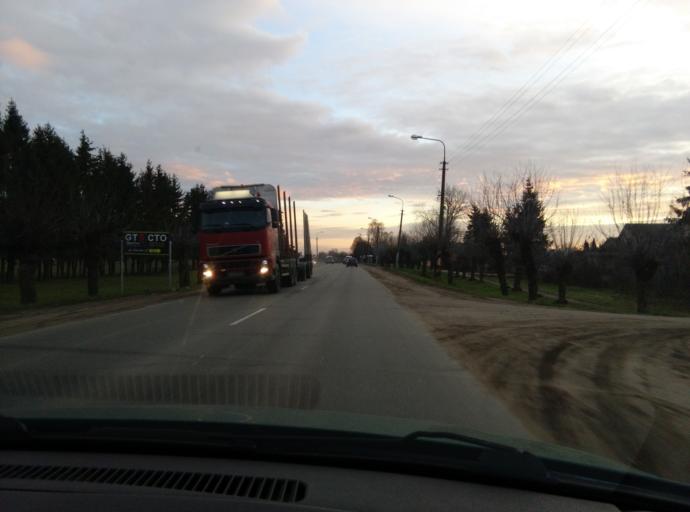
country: BY
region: Minsk
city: Horad Barysaw
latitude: 54.2681
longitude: 28.4988
